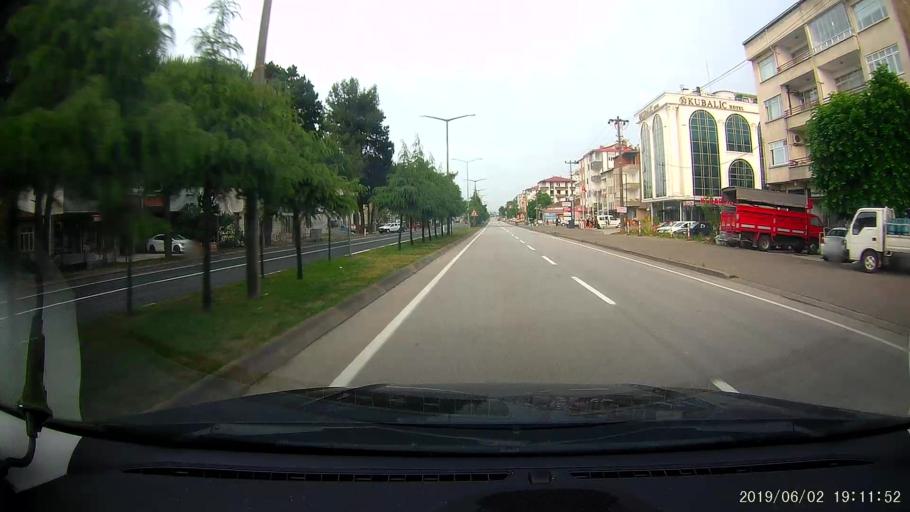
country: TR
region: Ordu
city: Gulyali
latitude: 40.9667
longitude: 38.0595
